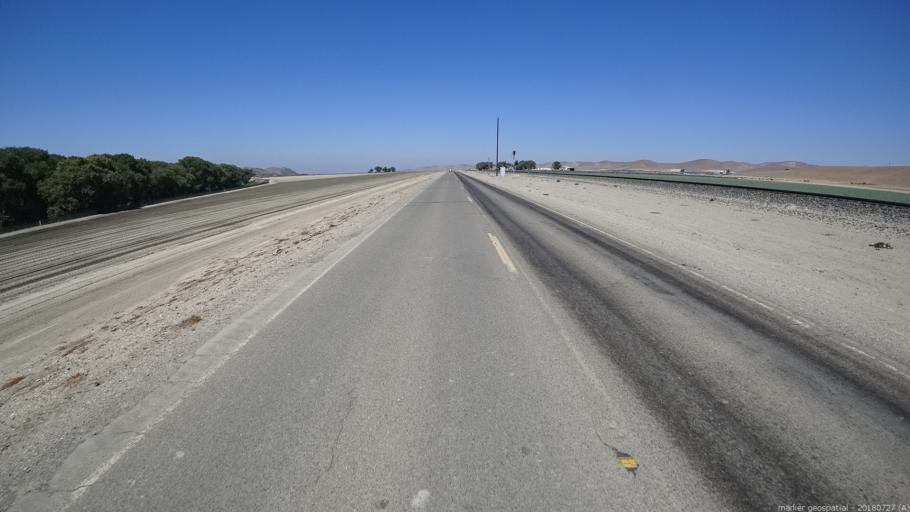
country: US
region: California
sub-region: Monterey County
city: King City
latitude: 36.0639
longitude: -120.9295
